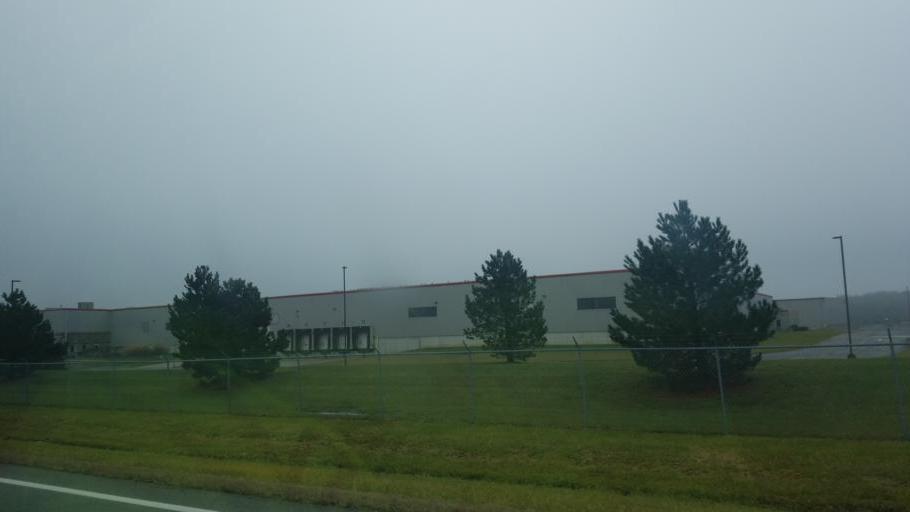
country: US
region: Ohio
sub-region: Champaign County
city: North Lewisburg
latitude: 40.2992
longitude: -83.5617
